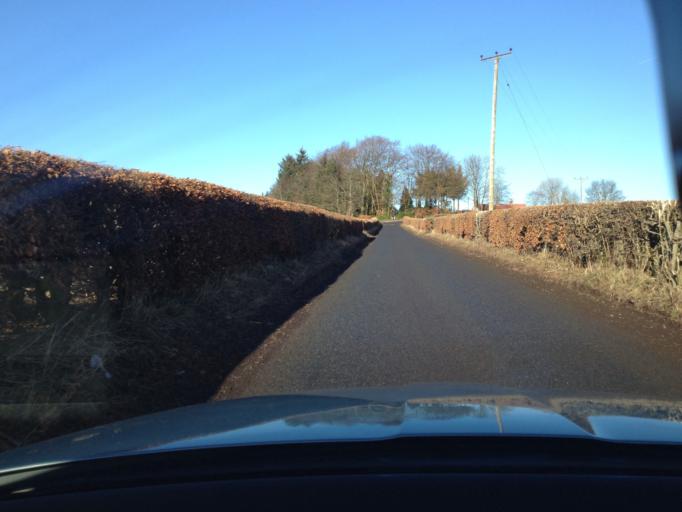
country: GB
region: Scotland
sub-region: Perth and Kinross
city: Bridge of Earn
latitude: 56.2885
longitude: -3.3951
